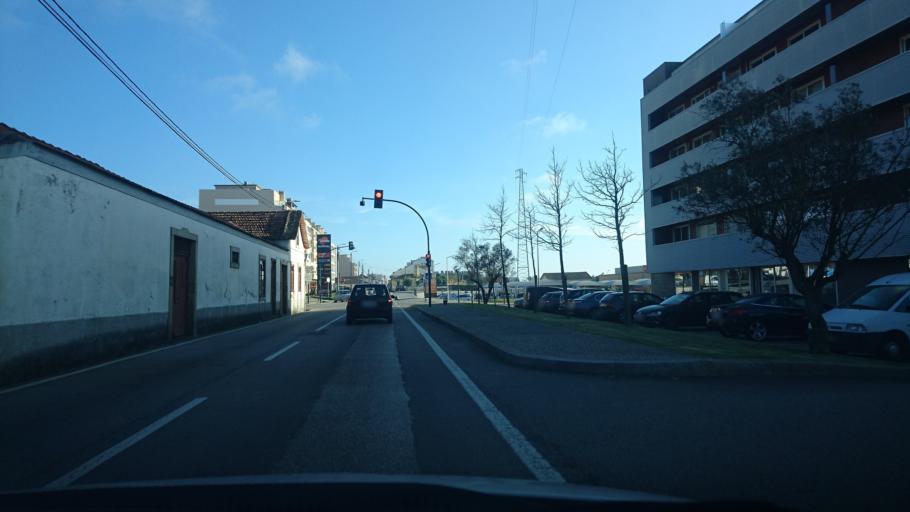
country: PT
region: Aveiro
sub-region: Ovar
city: Esmoriz
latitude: 40.9626
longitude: -8.6285
